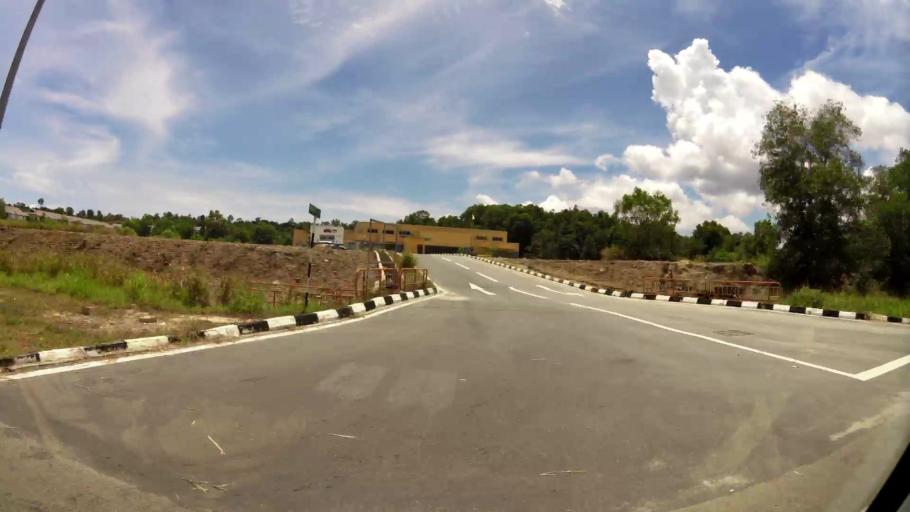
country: BN
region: Brunei and Muara
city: Bandar Seri Begawan
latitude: 4.9665
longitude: 114.9122
